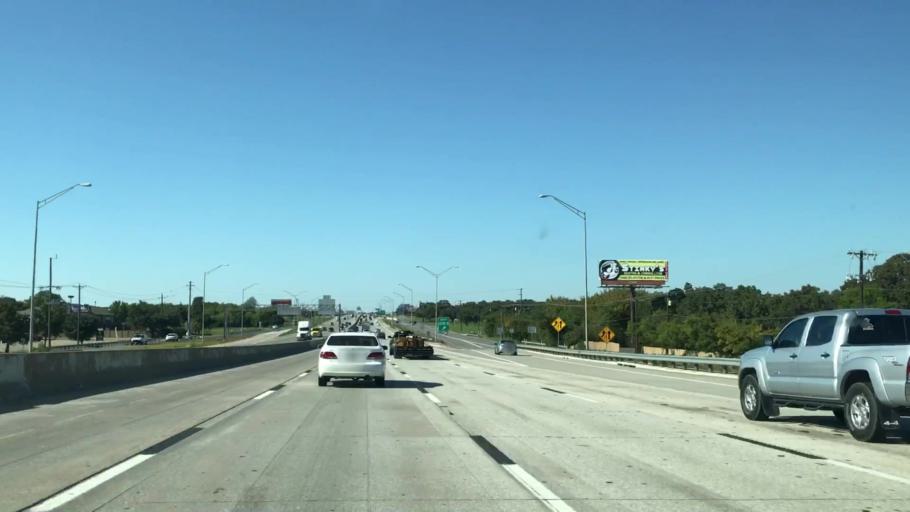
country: US
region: Texas
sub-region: Denton County
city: Hickory Creek
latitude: 33.1325
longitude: -97.0420
